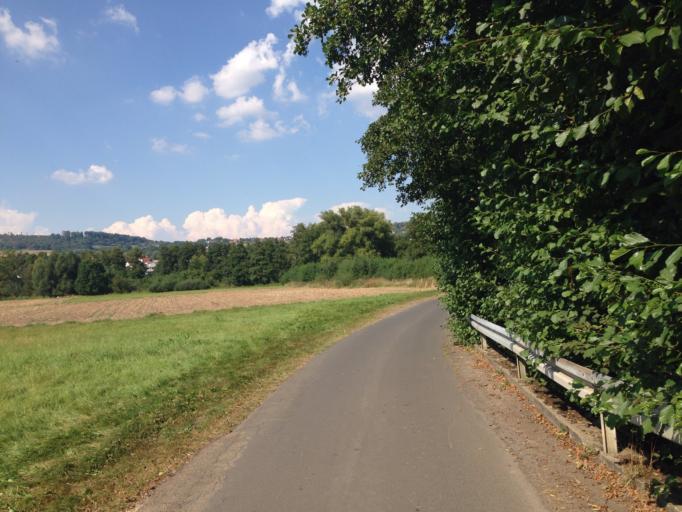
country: DE
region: Hesse
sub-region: Regierungsbezirk Giessen
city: Rabenau
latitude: 50.6741
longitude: 8.8317
